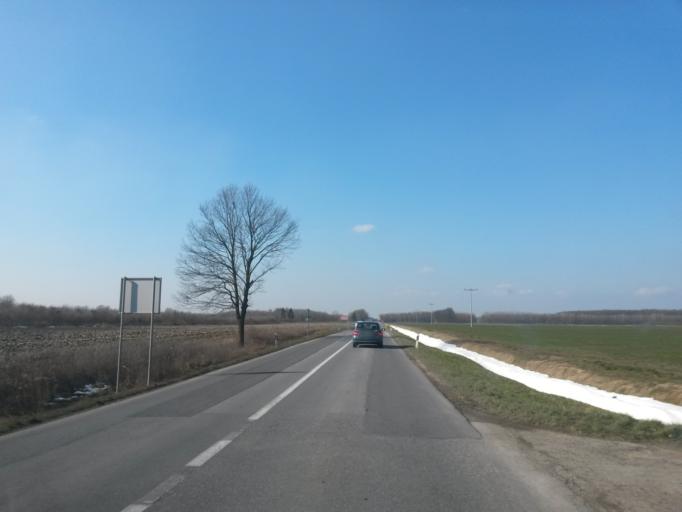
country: HR
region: Osjecko-Baranjska
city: Ladimirevci
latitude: 45.6304
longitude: 18.4896
